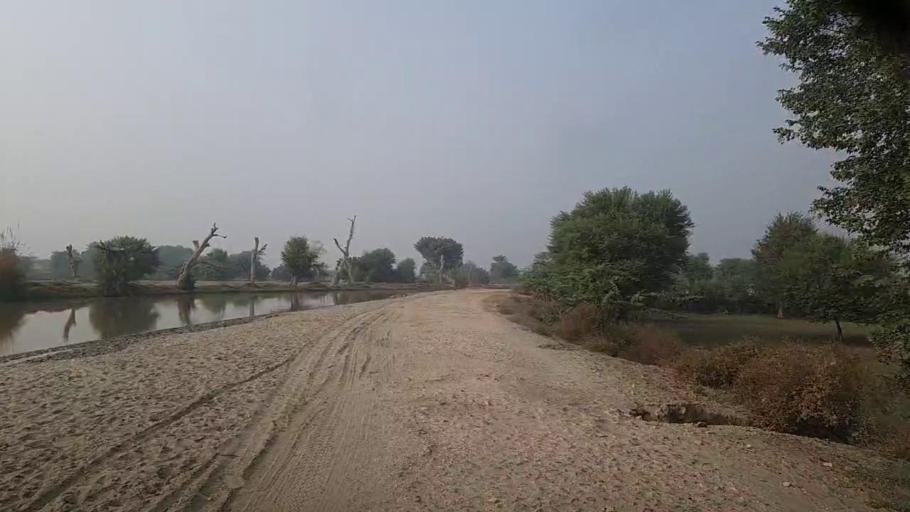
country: PK
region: Sindh
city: Bozdar
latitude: 27.1510
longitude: 68.6608
